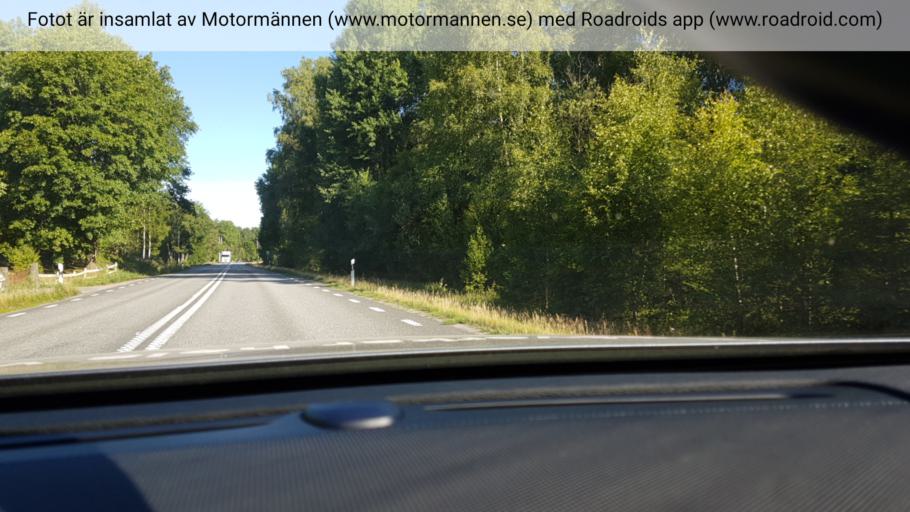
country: SE
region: Kronoberg
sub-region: Markaryds Kommun
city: Markaryd
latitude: 56.4371
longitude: 13.6126
